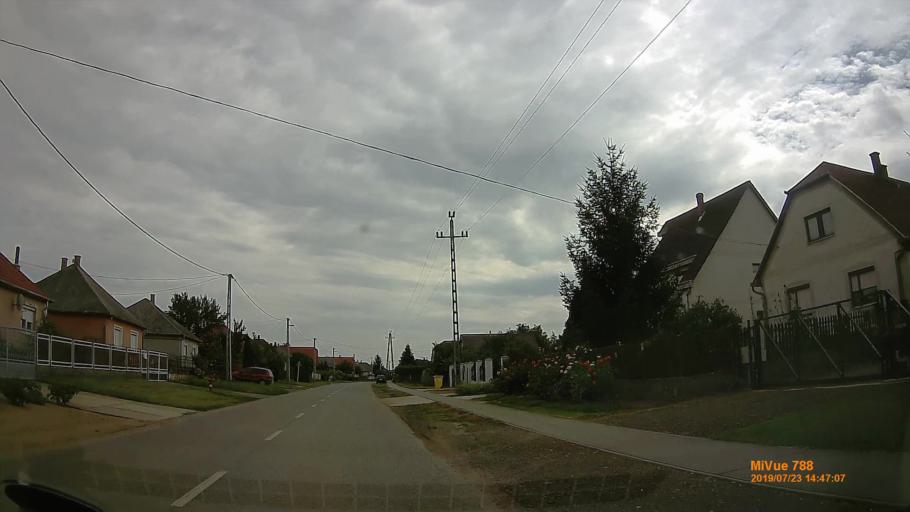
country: HU
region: Szabolcs-Szatmar-Bereg
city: Nyiregyhaza
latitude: 47.9133
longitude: 21.6754
